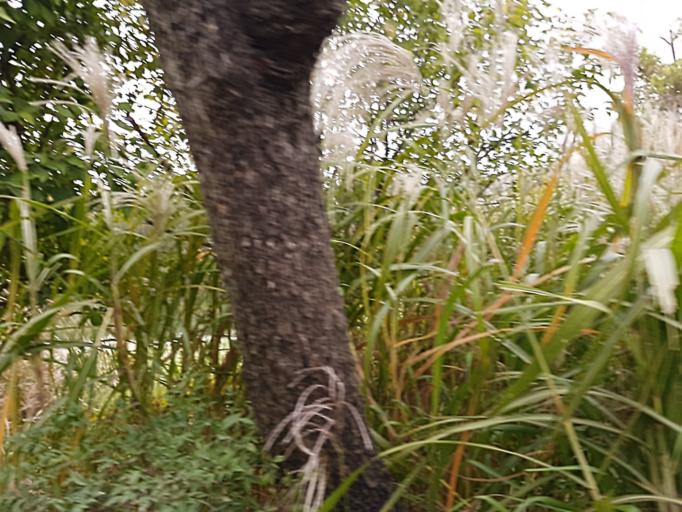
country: CN
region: Zhejiang Sheng
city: Cangqian
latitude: 30.2806
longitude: 120.0220
